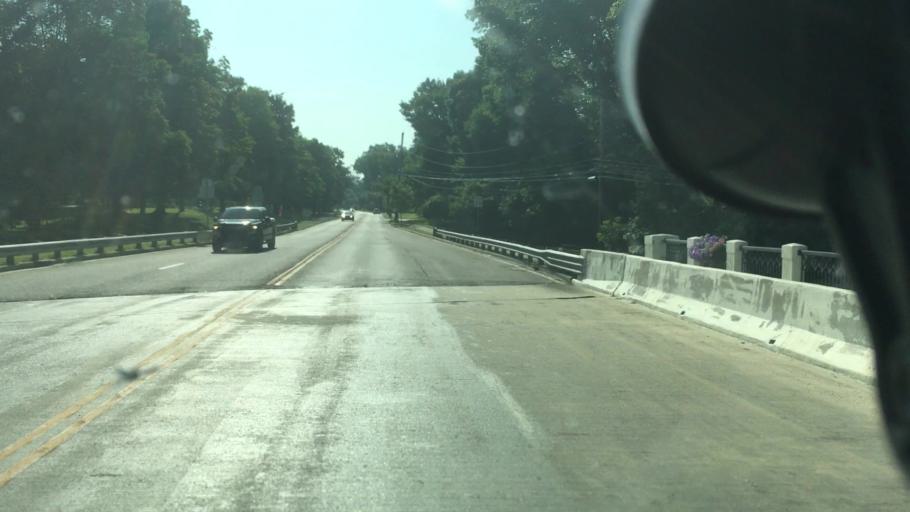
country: US
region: Ohio
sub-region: Mahoning County
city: Poland
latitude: 41.0239
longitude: -80.6104
